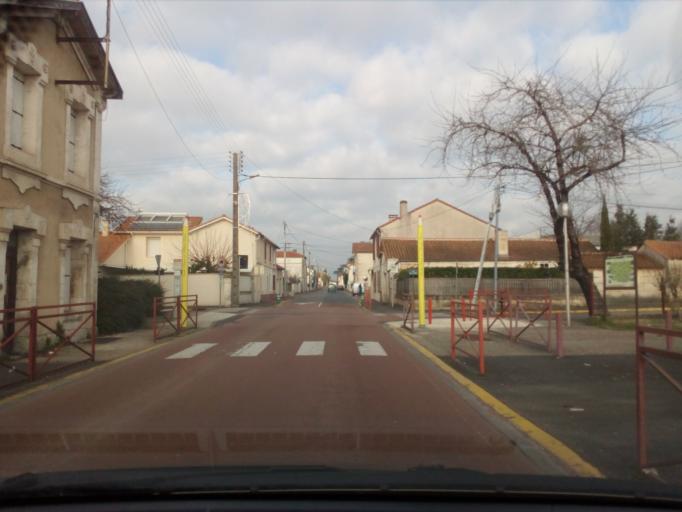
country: FR
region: Poitou-Charentes
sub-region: Departement de la Charente
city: Gond-Pontouvre
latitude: 45.6780
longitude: 0.1553
